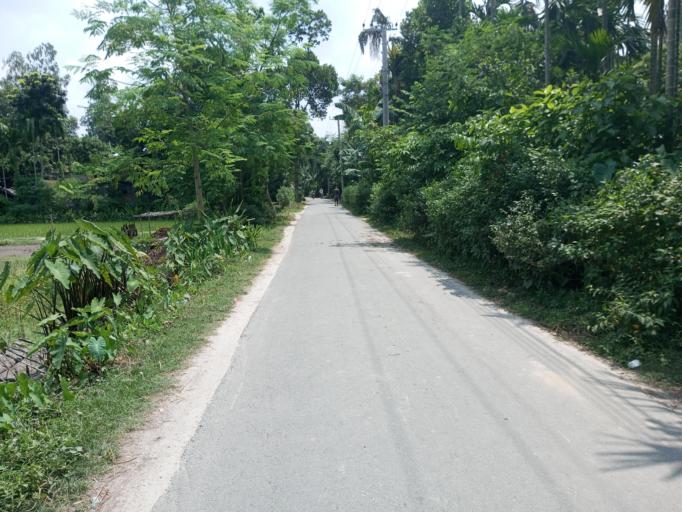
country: BD
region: Rangpur Division
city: Lalmanirhat
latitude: 25.9554
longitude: 89.2669
